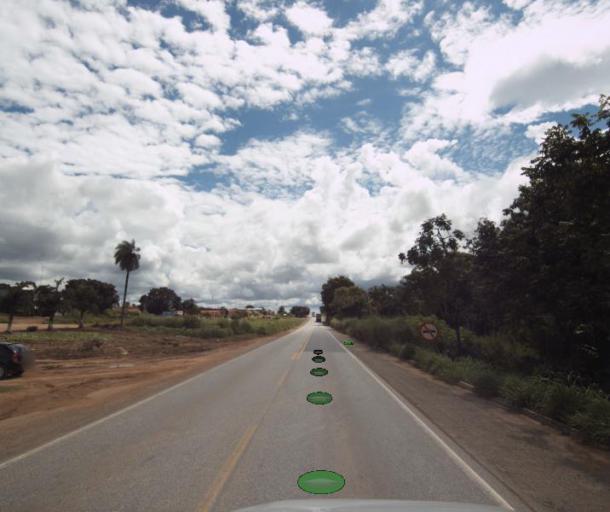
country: BR
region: Goias
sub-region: Uruacu
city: Uruacu
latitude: -14.3202
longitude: -49.1513
